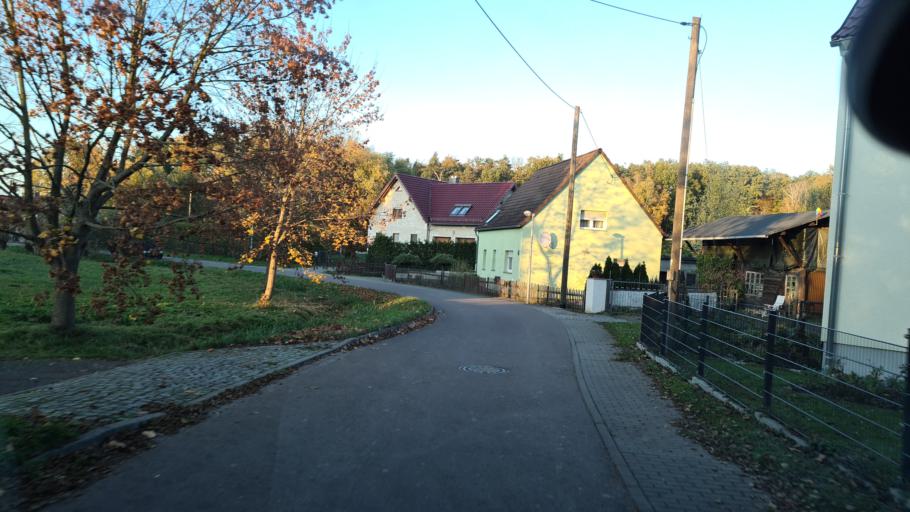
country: DE
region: Saxony
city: Schildau
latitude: 51.4327
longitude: 12.9745
